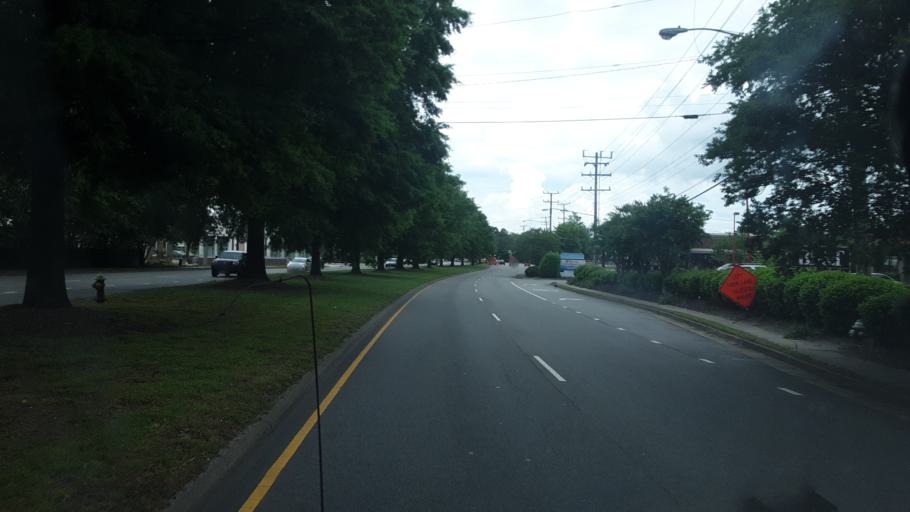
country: US
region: Virginia
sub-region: City of Virginia Beach
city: Virginia Beach
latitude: 36.7666
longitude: -76.0140
